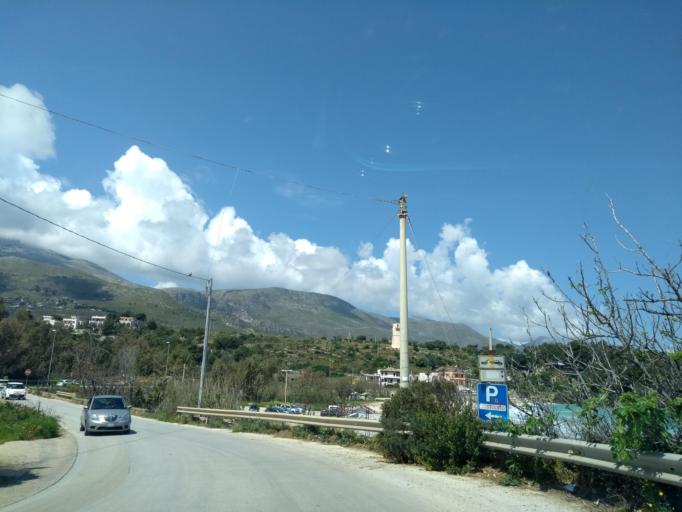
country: IT
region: Sicily
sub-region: Trapani
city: Castellammare del Golfo
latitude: 38.0559
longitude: 12.8411
